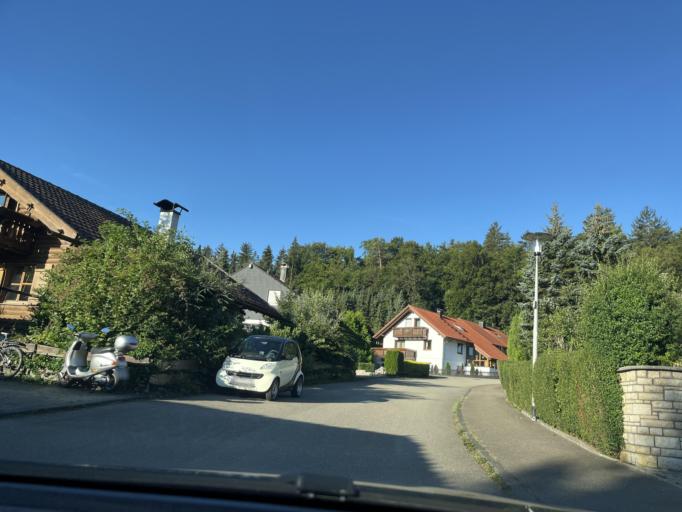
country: DE
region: Baden-Wuerttemberg
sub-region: Tuebingen Region
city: Gammertingen
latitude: 48.2404
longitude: 9.2089
